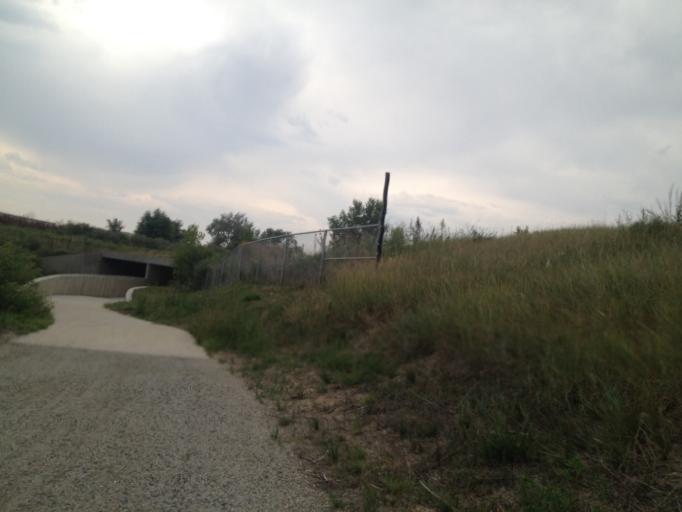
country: US
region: Colorado
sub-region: Boulder County
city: Erie
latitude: 40.0108
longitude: -105.0524
